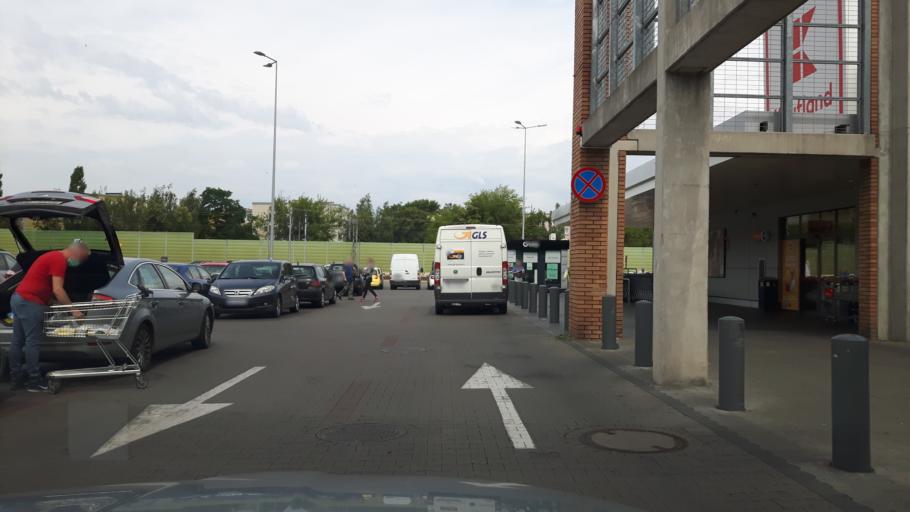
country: PL
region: Masovian Voivodeship
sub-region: Powiat wolominski
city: Wolomin
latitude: 52.3482
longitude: 21.2443
